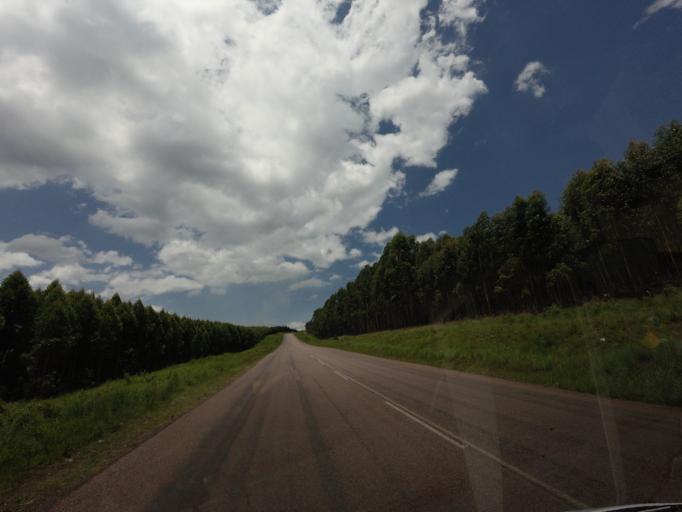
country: ZA
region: Mpumalanga
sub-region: Ehlanzeni District
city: Graksop
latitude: -25.0718
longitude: 30.8026
